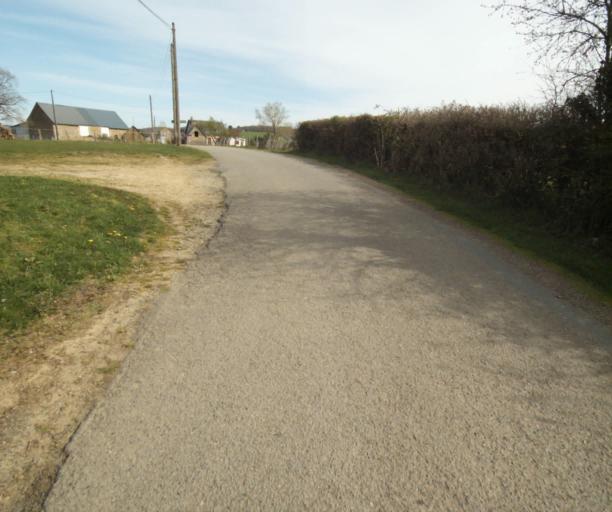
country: FR
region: Limousin
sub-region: Departement de la Correze
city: Correze
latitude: 45.3844
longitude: 1.8225
